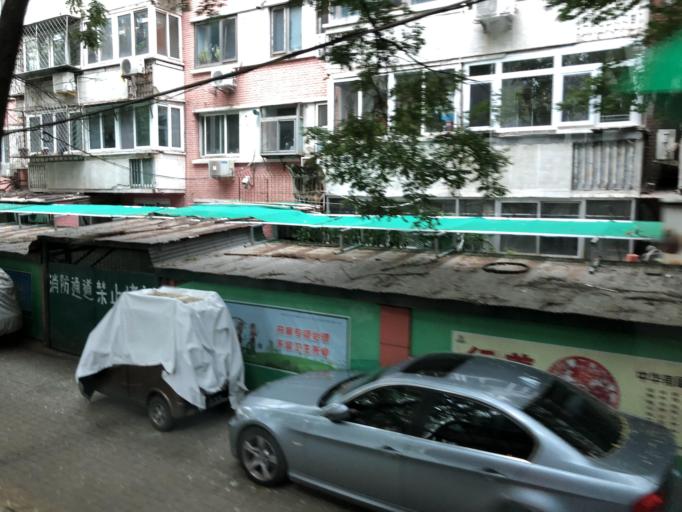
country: CN
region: Beijing
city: Jinrongjie
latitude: 39.9509
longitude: 116.3280
